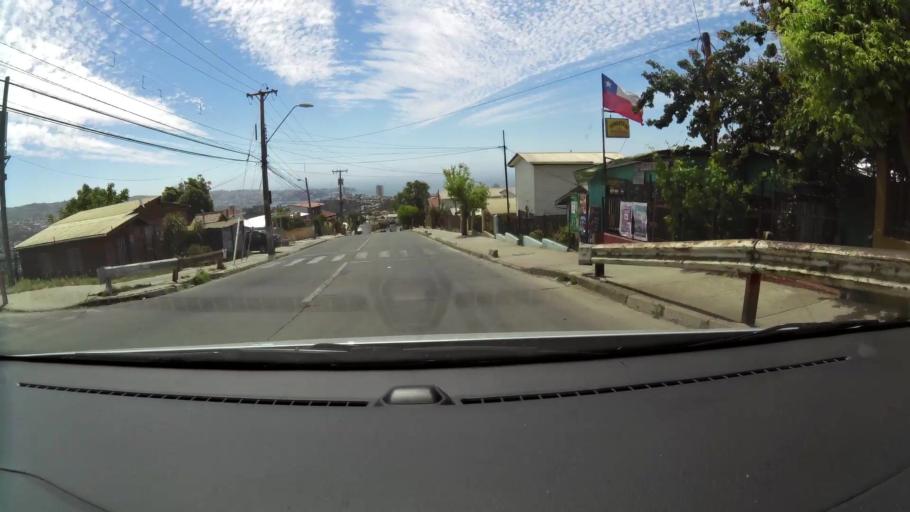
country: CL
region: Valparaiso
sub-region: Provincia de Valparaiso
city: Vina del Mar
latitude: -33.0605
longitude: -71.5743
